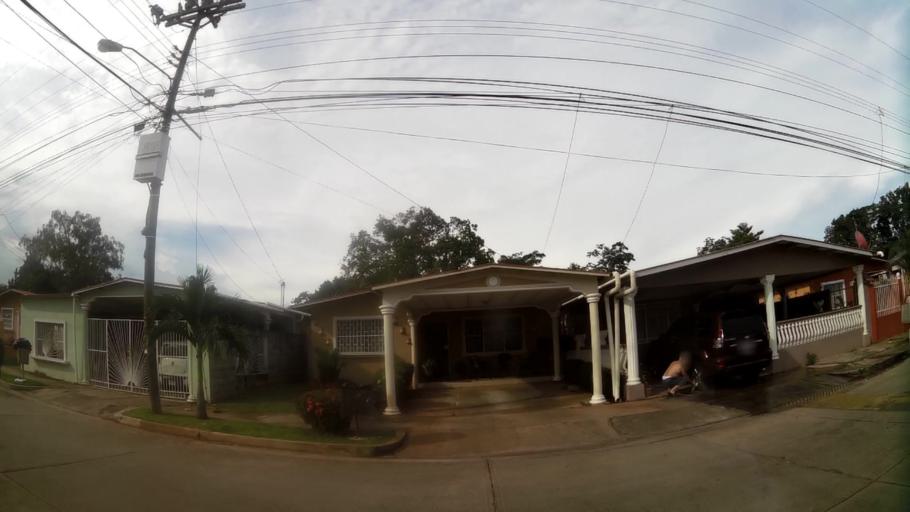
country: PA
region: Panama
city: La Chorrera
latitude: 8.8832
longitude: -79.7638
